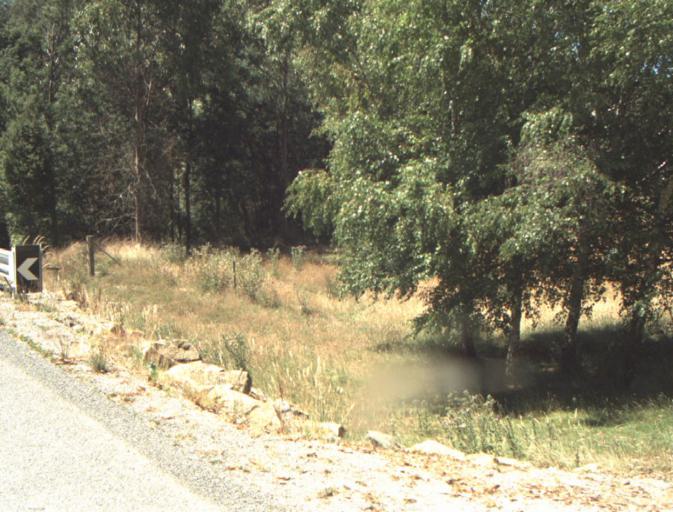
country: AU
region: Tasmania
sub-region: Dorset
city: Scottsdale
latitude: -41.2938
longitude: 147.4069
